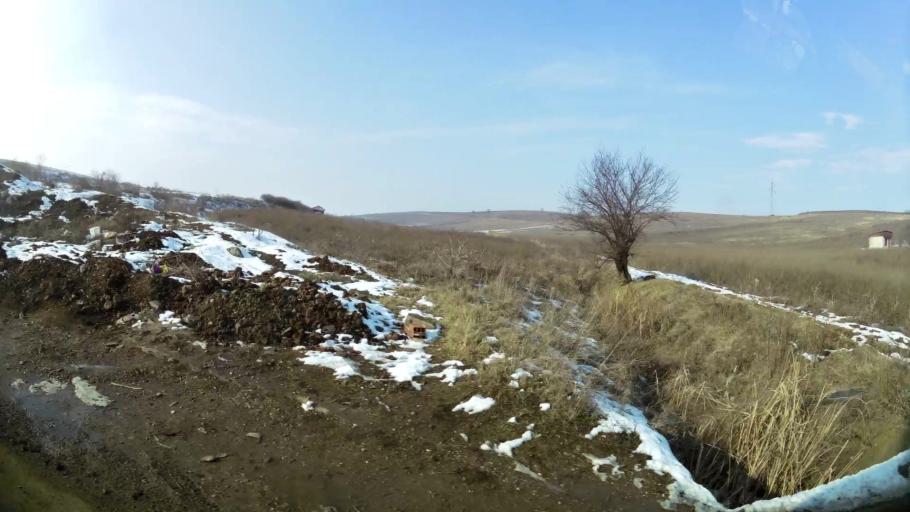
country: MK
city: Creshevo
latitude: 42.0156
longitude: 21.4907
